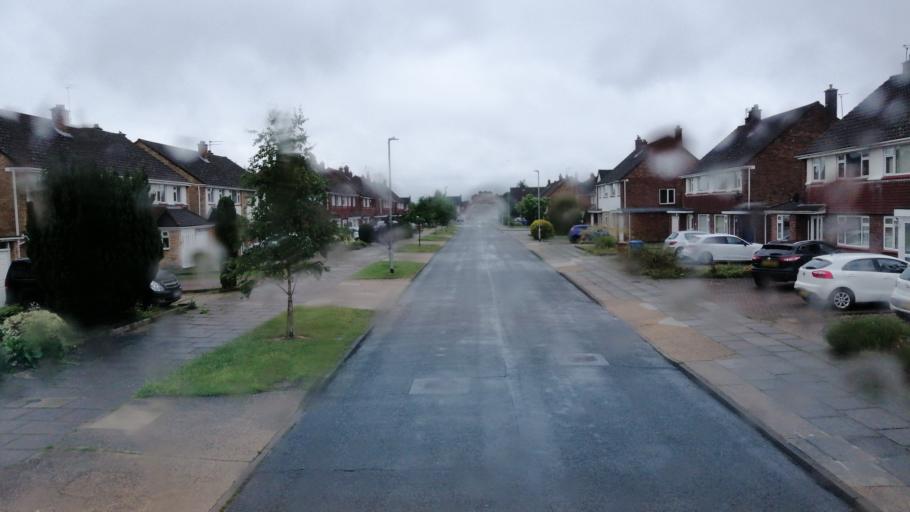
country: GB
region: England
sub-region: Suffolk
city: Kesgrave
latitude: 52.0476
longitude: 1.2049
